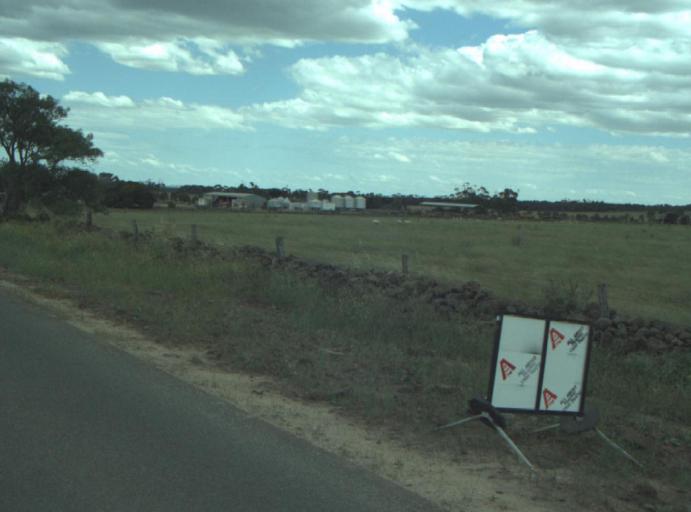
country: AU
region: Victoria
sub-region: Wyndham
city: Little River
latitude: -37.9477
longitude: 144.4656
